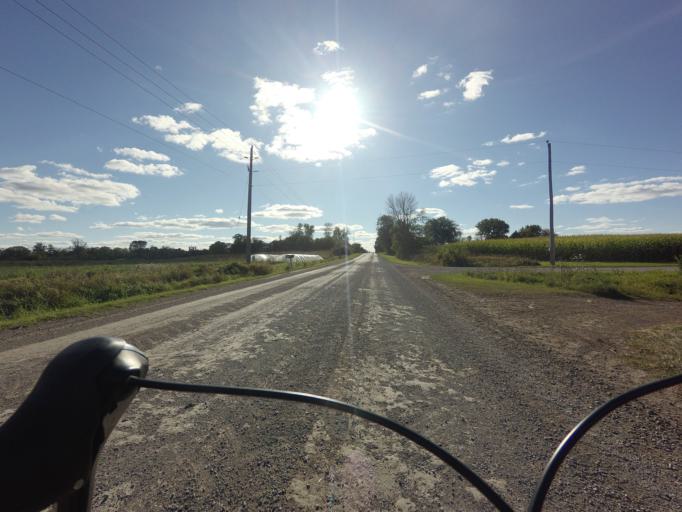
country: CA
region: Ontario
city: Bells Corners
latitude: 45.1233
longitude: -75.6838
